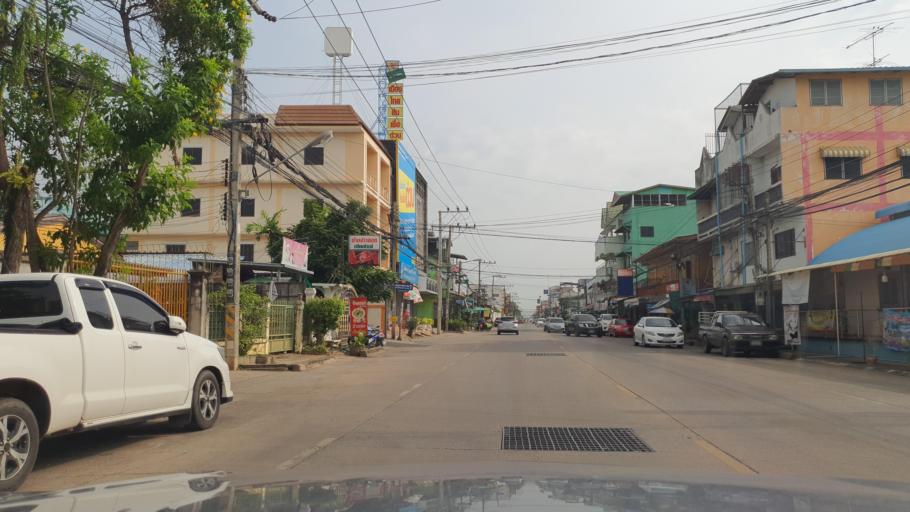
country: TH
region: Phitsanulok
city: Phitsanulok
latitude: 16.8321
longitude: 100.2655
